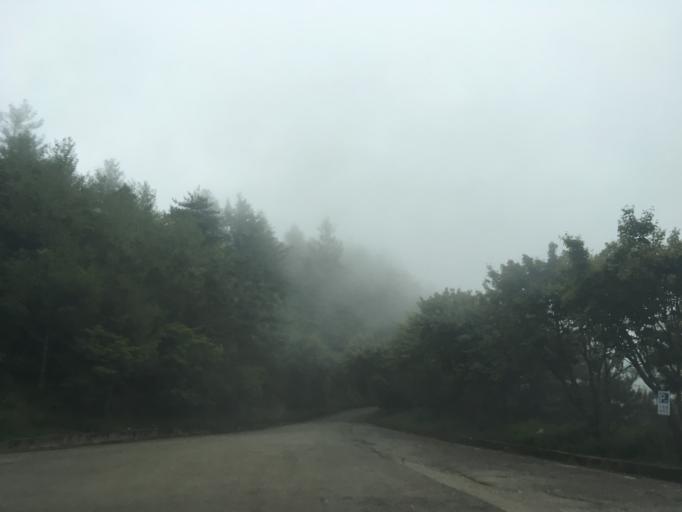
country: TW
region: Taiwan
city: Fengyuan
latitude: 24.2792
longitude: 121.0268
